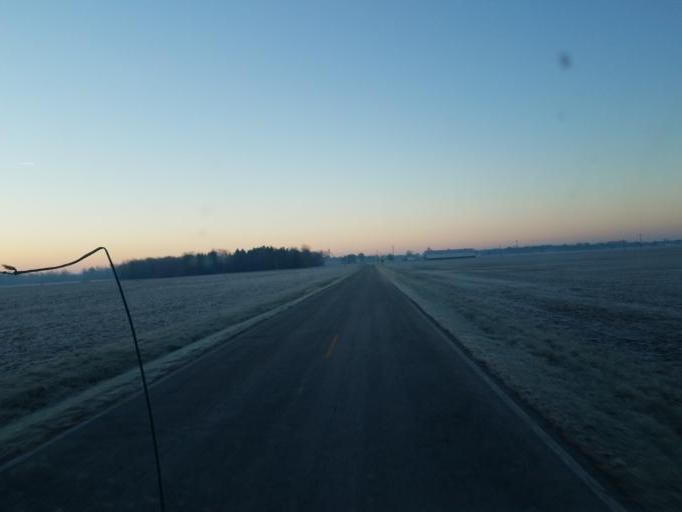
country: US
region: Ohio
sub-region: Marion County
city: Marion
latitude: 40.5306
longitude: -83.0249
